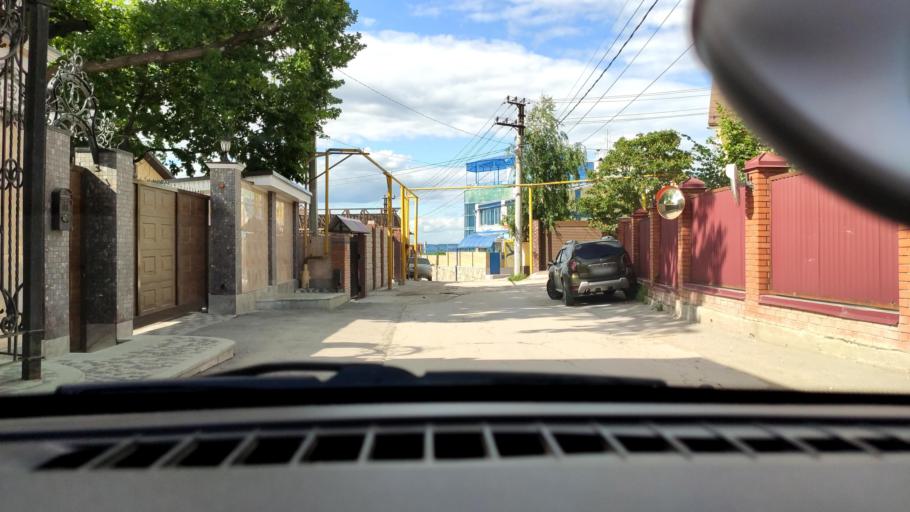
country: RU
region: Samara
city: Samara
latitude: 53.2412
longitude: 50.1692
